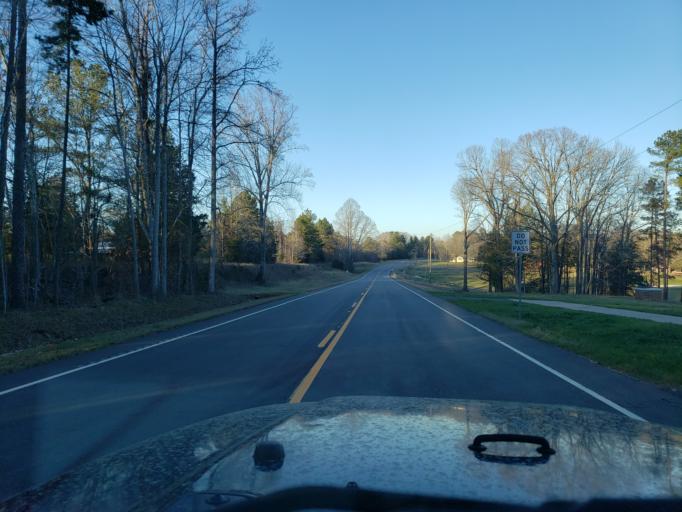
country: US
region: South Carolina
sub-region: Cherokee County
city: Blacksburg
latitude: 35.0174
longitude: -81.4063
